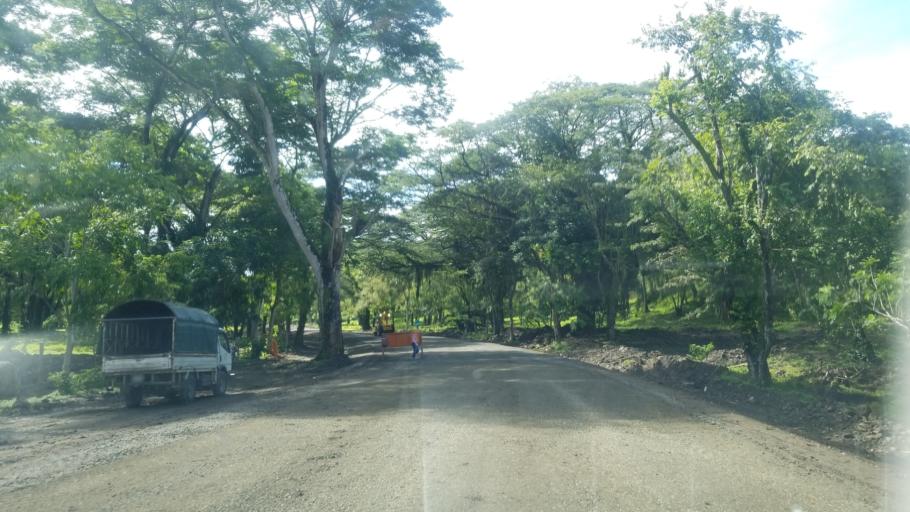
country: CR
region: Alajuela
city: San Jose
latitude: 11.0972
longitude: -85.2677
